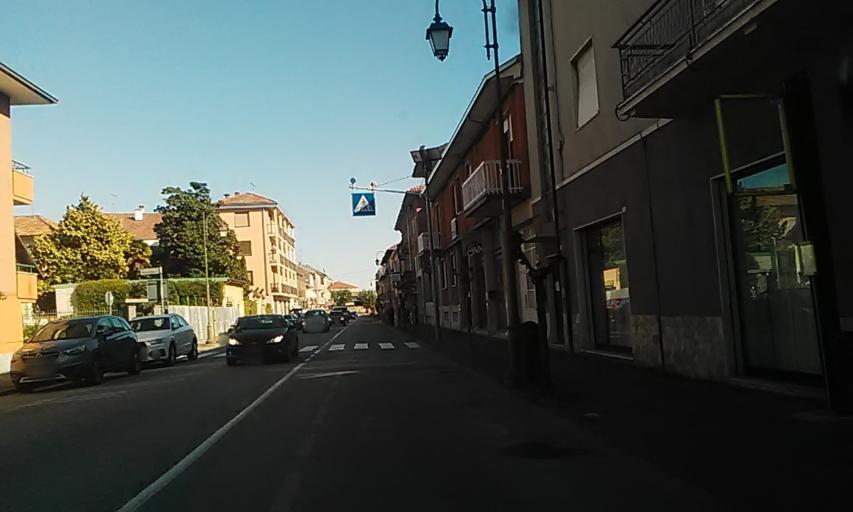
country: IT
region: Piedmont
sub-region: Provincia di Novara
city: Romagnano Sesia
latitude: 45.6324
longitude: 8.3816
